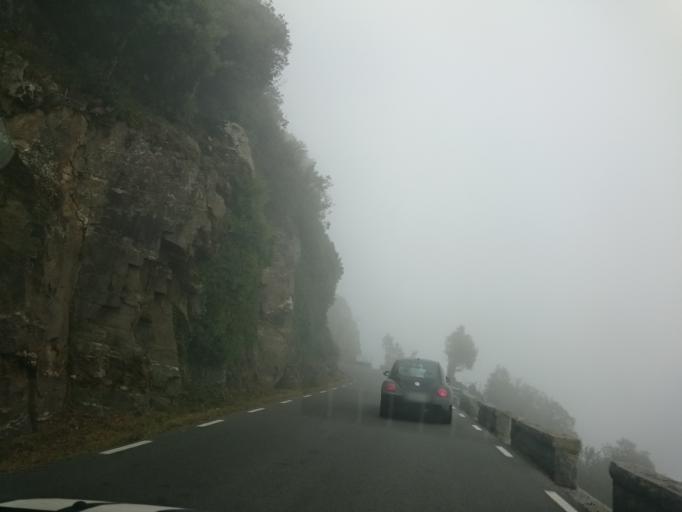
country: ES
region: Catalonia
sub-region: Provincia de Barcelona
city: Fogars de Montclus
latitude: 41.7554
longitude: 2.4724
